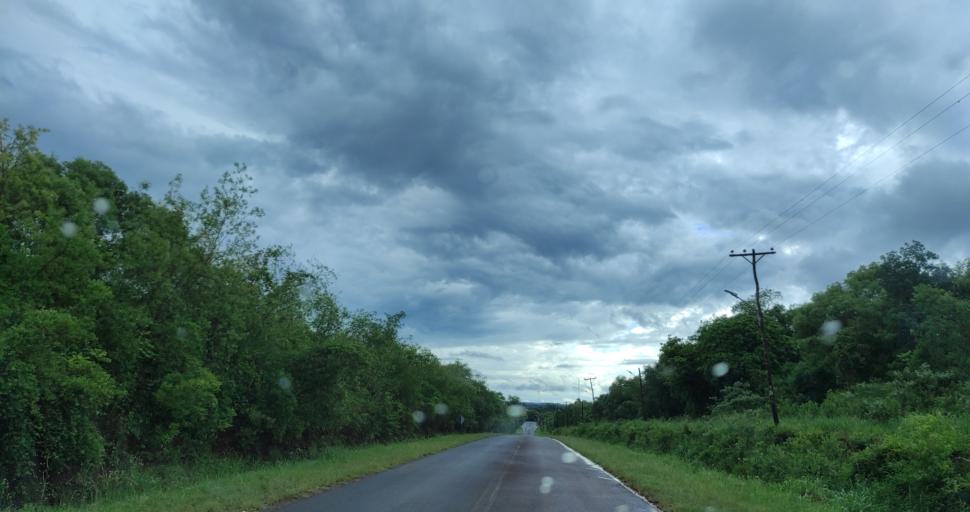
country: AR
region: Misiones
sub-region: Departamento de Apostoles
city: San Jose
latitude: -27.7720
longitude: -55.7631
